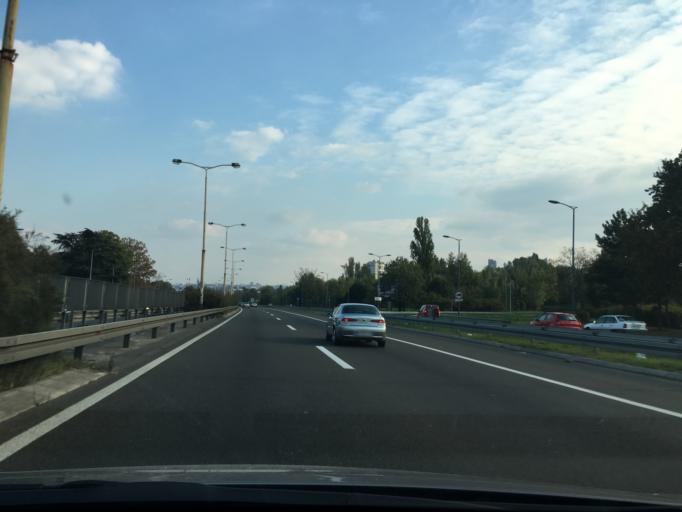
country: RS
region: Central Serbia
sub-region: Belgrade
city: Vracar
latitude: 44.7910
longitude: 20.4675
